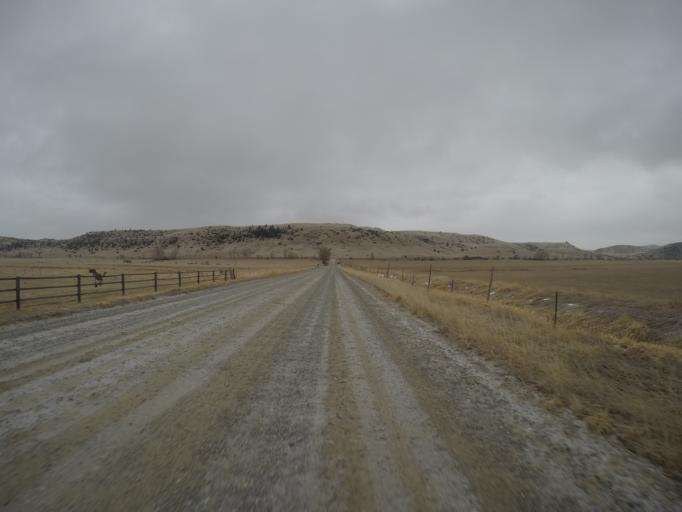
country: US
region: Montana
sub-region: Stillwater County
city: Absarokee
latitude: 45.5262
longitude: -109.4698
